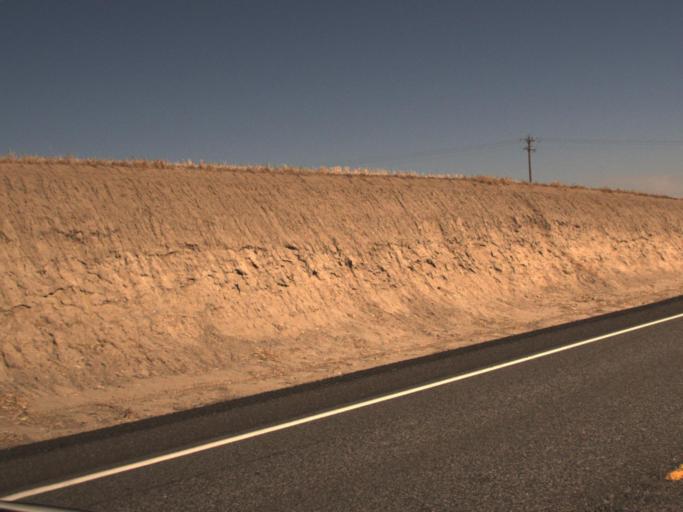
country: US
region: Washington
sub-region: Walla Walla County
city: Garrett
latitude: 46.2963
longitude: -118.6178
